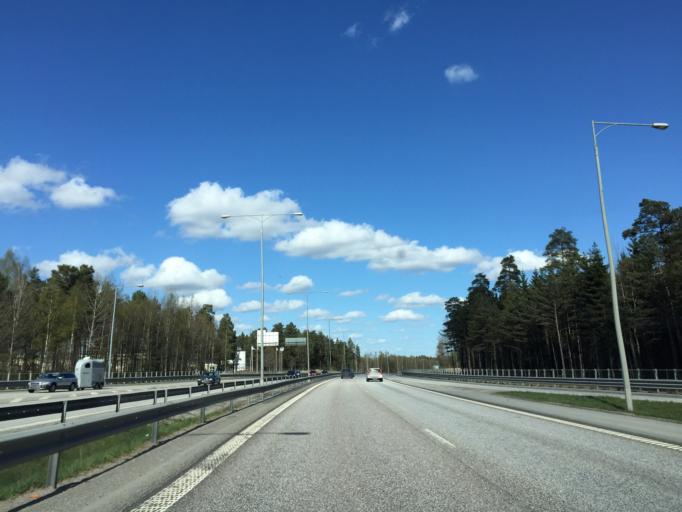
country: SE
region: OErebro
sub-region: Orebro Kommun
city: Orebro
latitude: 59.2468
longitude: 15.1478
